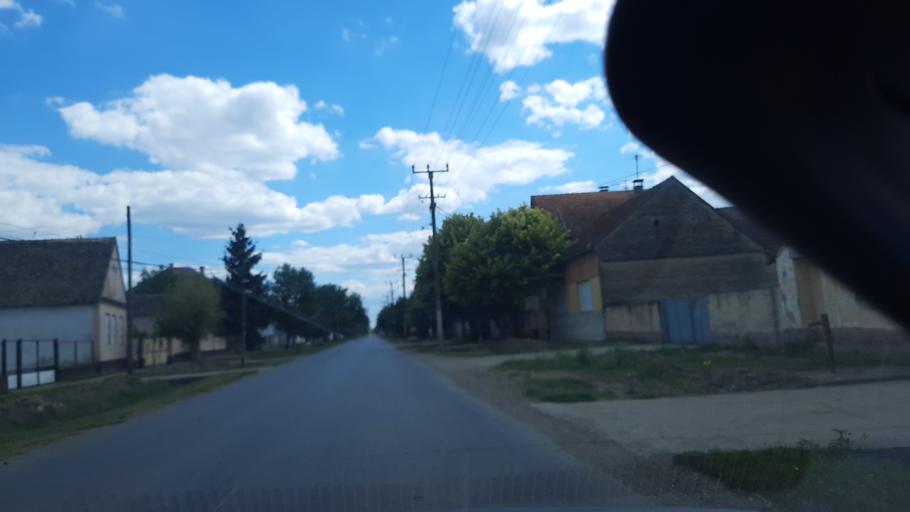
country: RS
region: Autonomna Pokrajina Vojvodina
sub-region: Sremski Okrug
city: Pecinci
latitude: 44.9325
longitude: 20.0071
